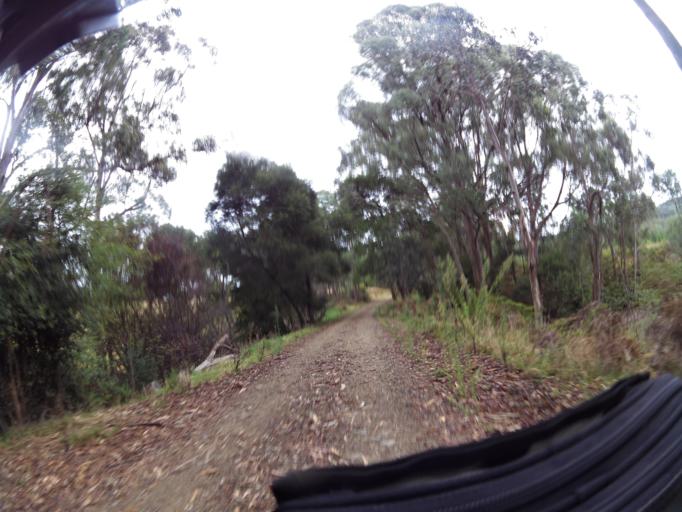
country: AU
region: New South Wales
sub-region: Greater Hume Shire
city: Holbrook
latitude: -36.1503
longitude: 147.4732
